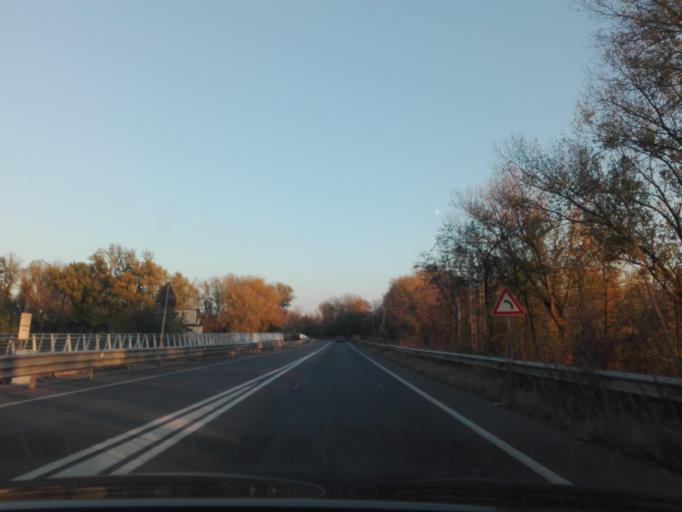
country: IT
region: Lombardy
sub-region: Provincia di Mantova
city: Lunetta-Frassino
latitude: 45.1446
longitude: 10.8113
